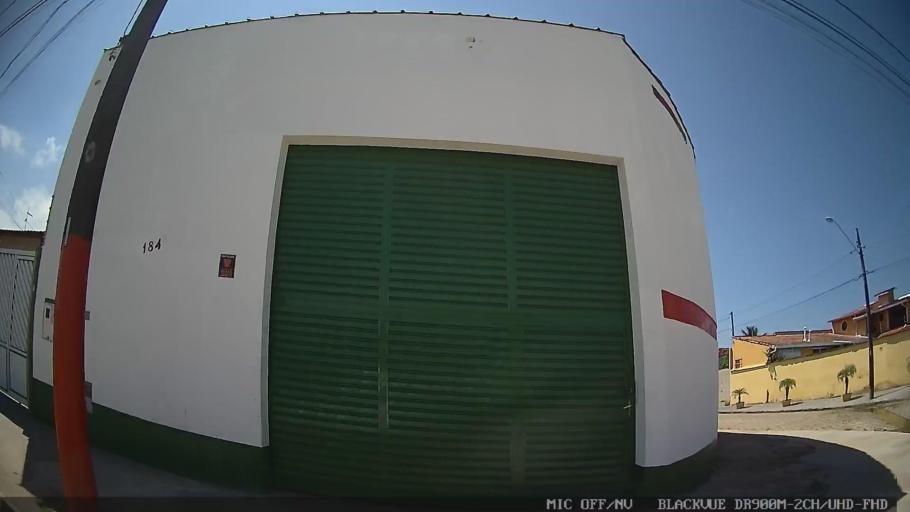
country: BR
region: Sao Paulo
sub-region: Peruibe
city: Peruibe
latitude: -24.3027
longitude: -46.9923
